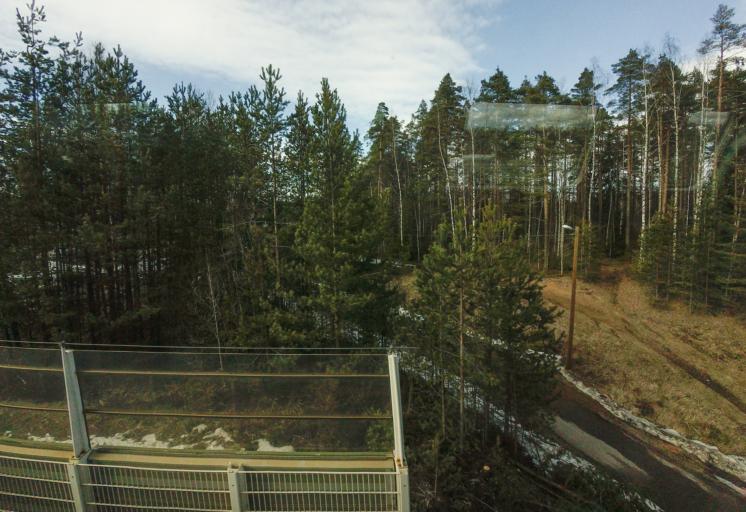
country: FI
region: South Karelia
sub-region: Lappeenranta
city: Joutseno
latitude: 61.1105
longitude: 28.4509
